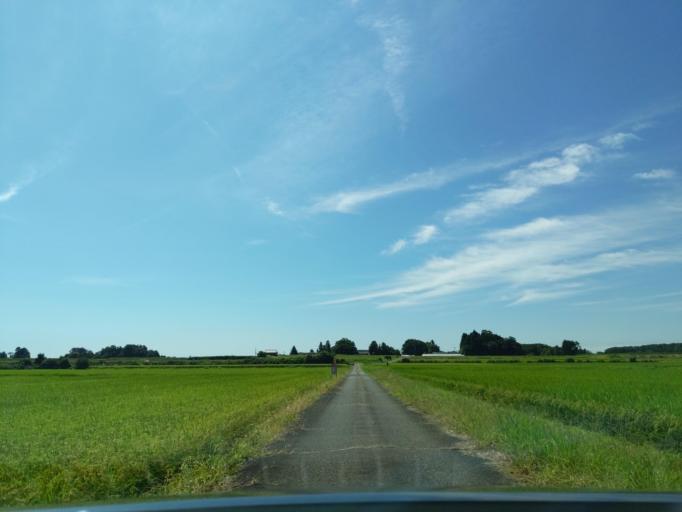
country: JP
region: Fukushima
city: Koriyama
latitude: 37.3708
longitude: 140.2830
